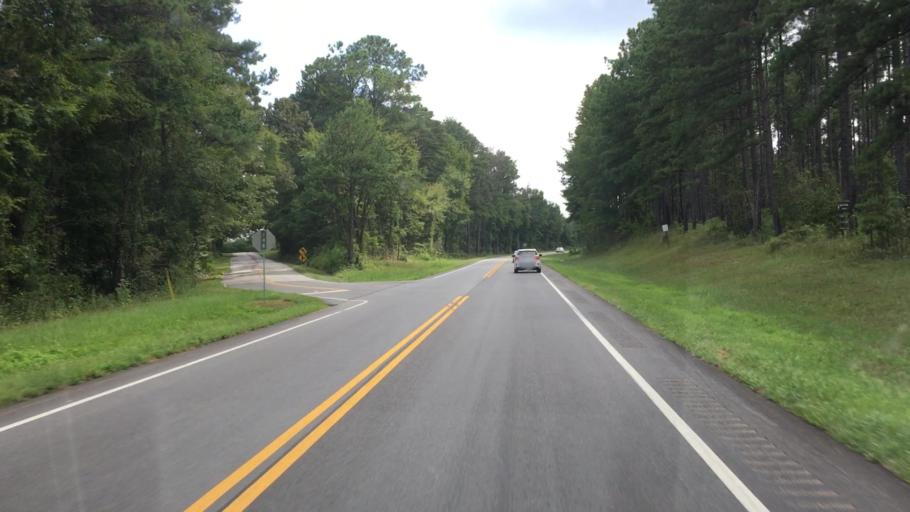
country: US
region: Georgia
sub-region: Putnam County
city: Eatonton
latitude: 33.3974
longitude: -83.3688
